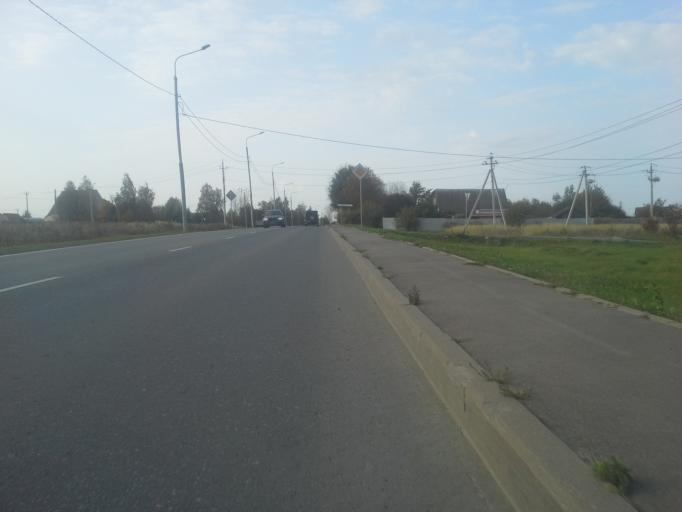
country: RU
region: Moskovskaya
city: Selyatino
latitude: 55.4482
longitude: 36.9457
